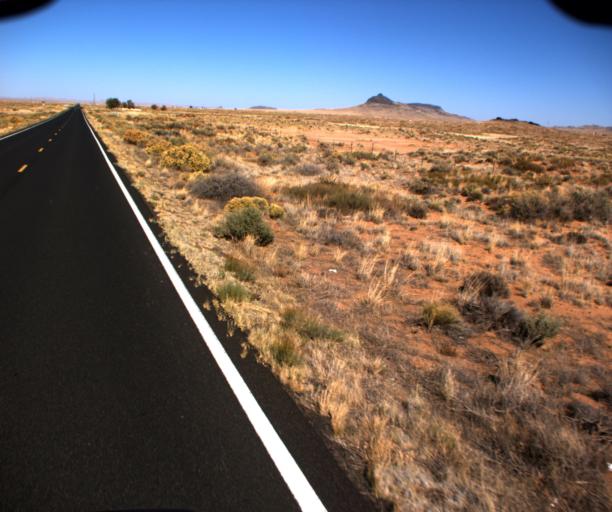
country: US
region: Arizona
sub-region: Navajo County
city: Dilkon
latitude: 35.4883
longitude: -110.4301
